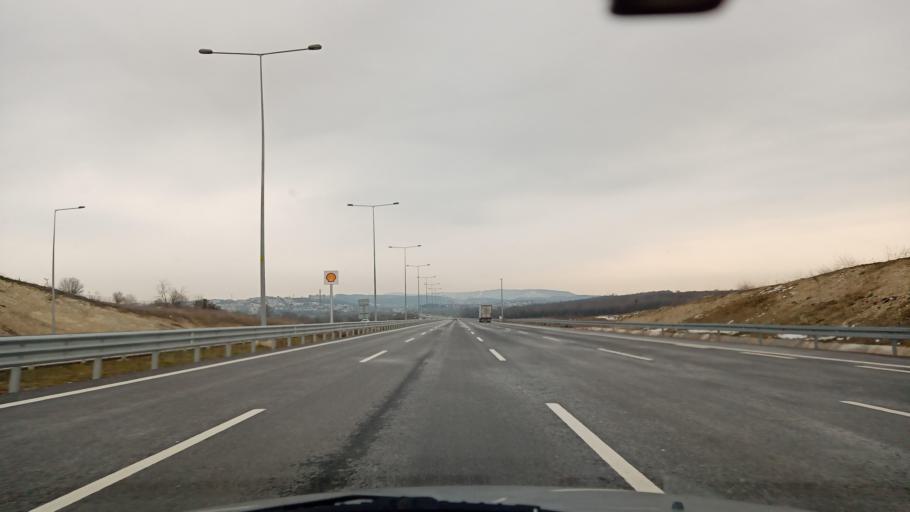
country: TR
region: Sakarya
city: Kazimpasa
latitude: 40.8437
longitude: 30.2940
